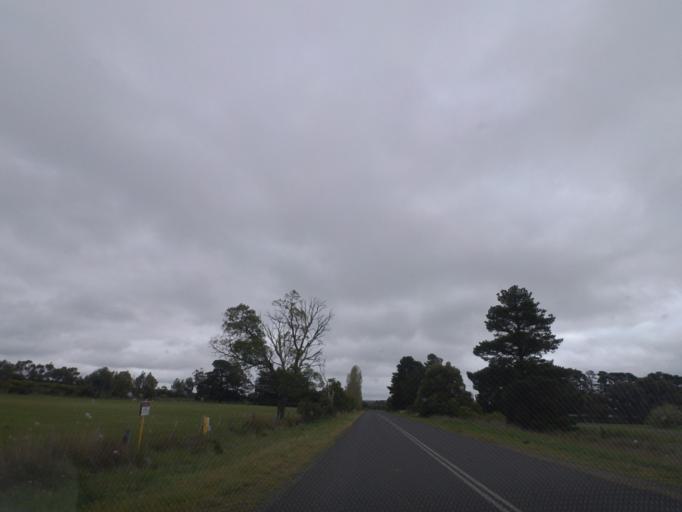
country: AU
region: Victoria
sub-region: Moorabool
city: Bacchus Marsh
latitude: -37.5934
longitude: 144.1836
